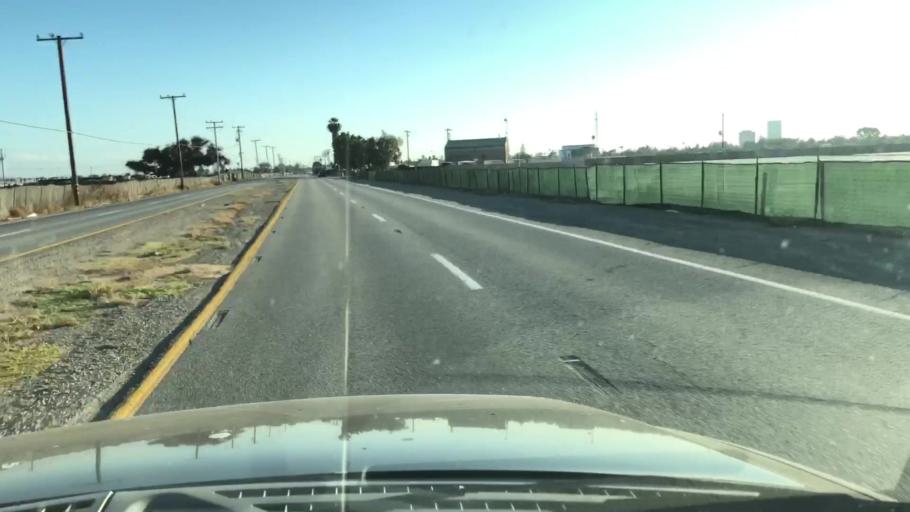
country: US
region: California
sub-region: Ventura County
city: El Rio
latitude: 34.2440
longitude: -119.1498
